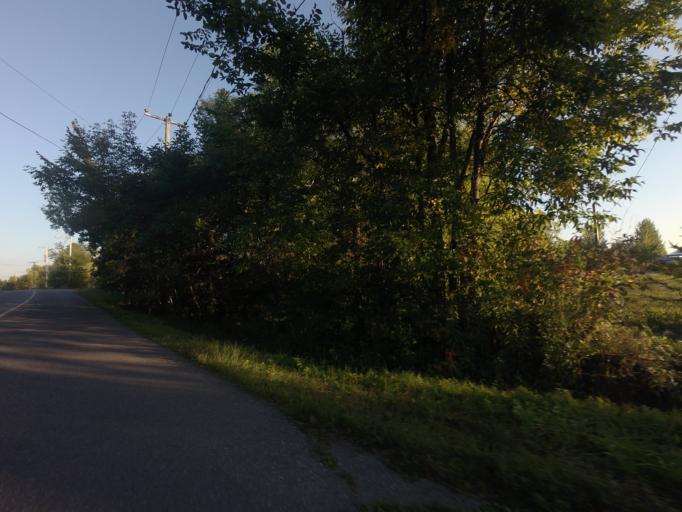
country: CA
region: Quebec
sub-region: Monteregie
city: Hudson
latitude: 45.4767
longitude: -74.1987
